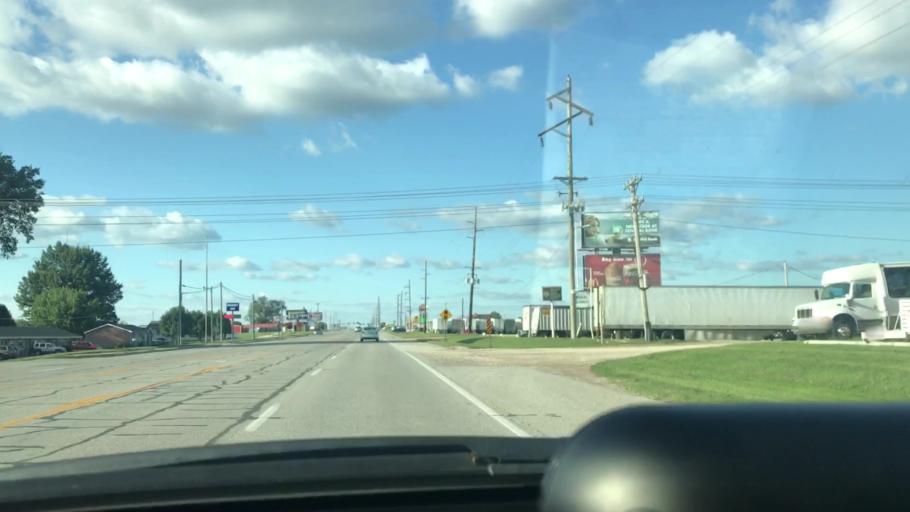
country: US
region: Missouri
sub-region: Pettis County
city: Sedalia
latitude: 38.6690
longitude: -93.2518
